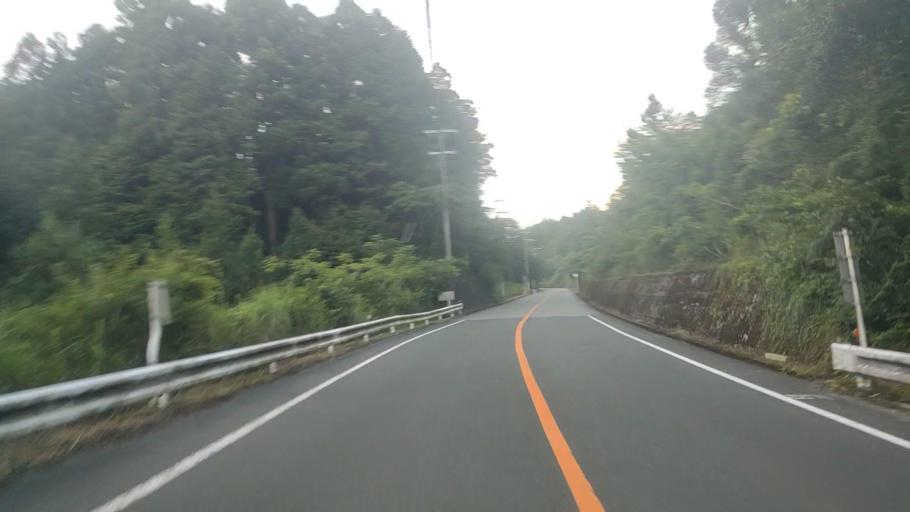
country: JP
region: Wakayama
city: Tanabe
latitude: 33.8167
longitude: 135.6178
